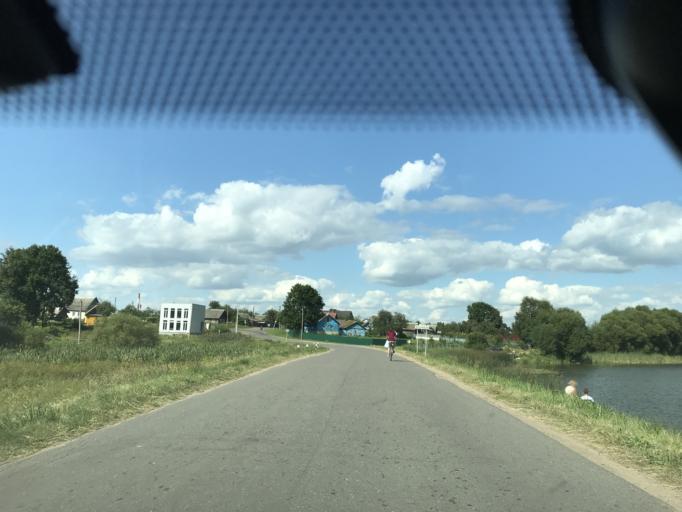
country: BY
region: Mogilev
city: Poselok Voskhod
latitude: 53.7807
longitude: 30.3490
